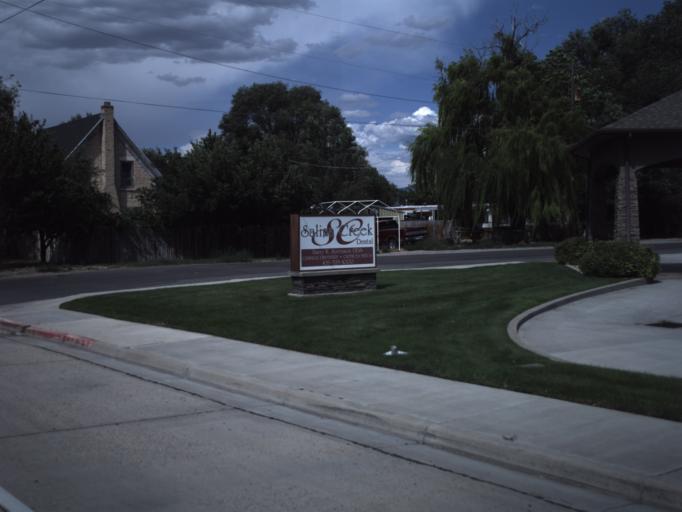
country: US
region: Utah
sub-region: Sevier County
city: Salina
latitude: 38.9601
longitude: -111.8600
